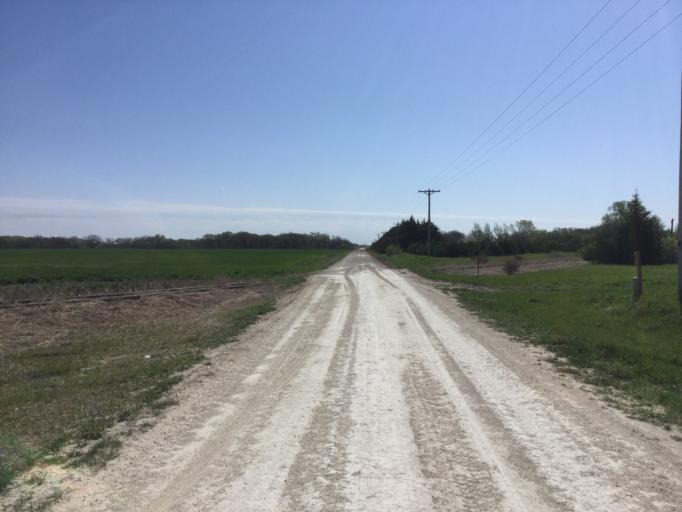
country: US
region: Kansas
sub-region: Osborne County
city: Osborne
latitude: 39.5240
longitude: -98.6064
